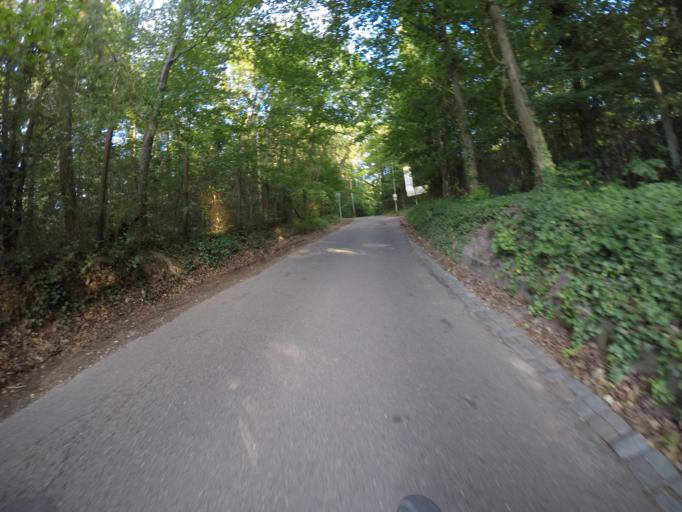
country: DE
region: Baden-Wuerttemberg
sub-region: Regierungsbezirk Stuttgart
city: Stuttgart-Ost
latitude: 48.7758
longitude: 9.2191
